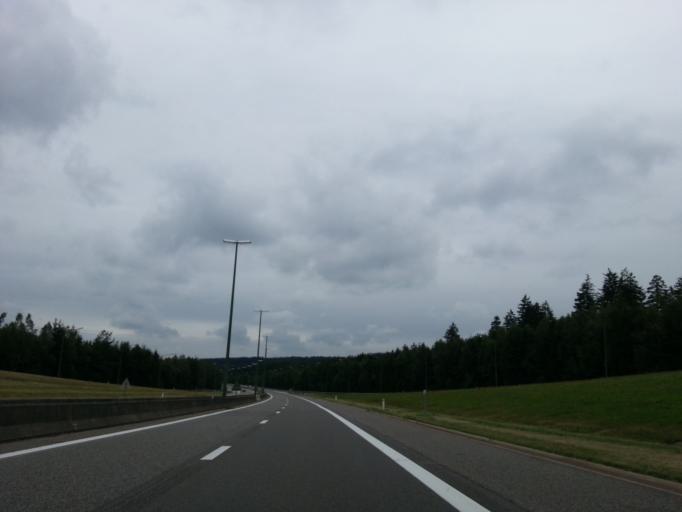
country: BE
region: Wallonia
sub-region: Province de Liege
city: Saint-Vith
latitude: 50.3394
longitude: 6.0885
